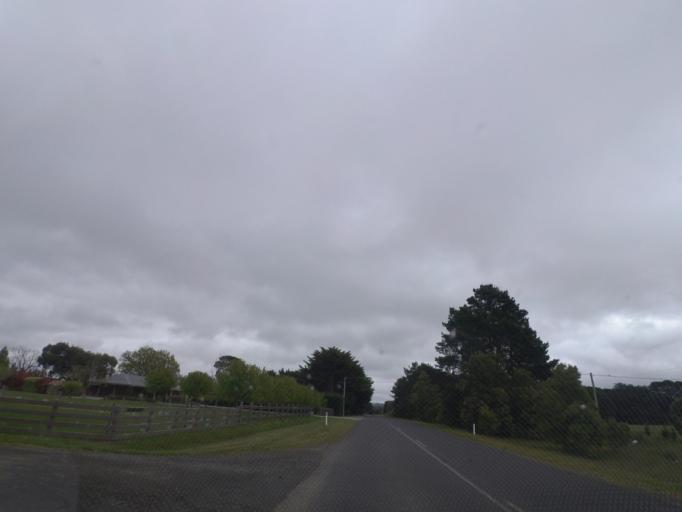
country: AU
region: Victoria
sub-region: Moorabool
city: Bacchus Marsh
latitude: -37.5942
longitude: 144.1882
